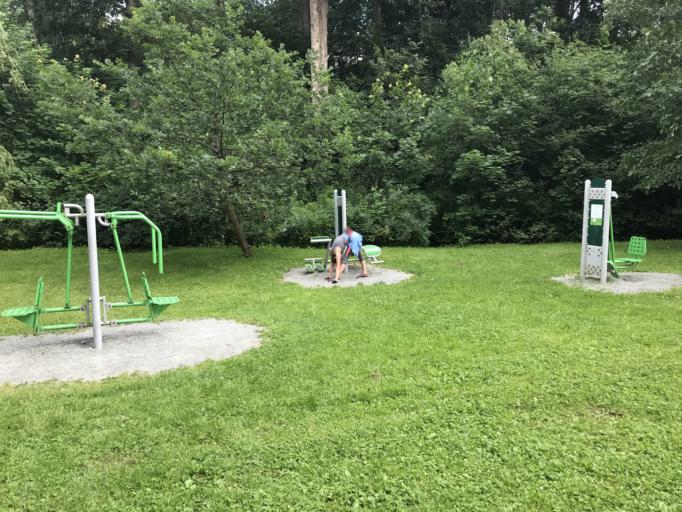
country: PL
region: Lower Silesian Voivodeship
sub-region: Powiat klodzki
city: Duszniki-Zdroj
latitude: 50.3890
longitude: 16.3792
